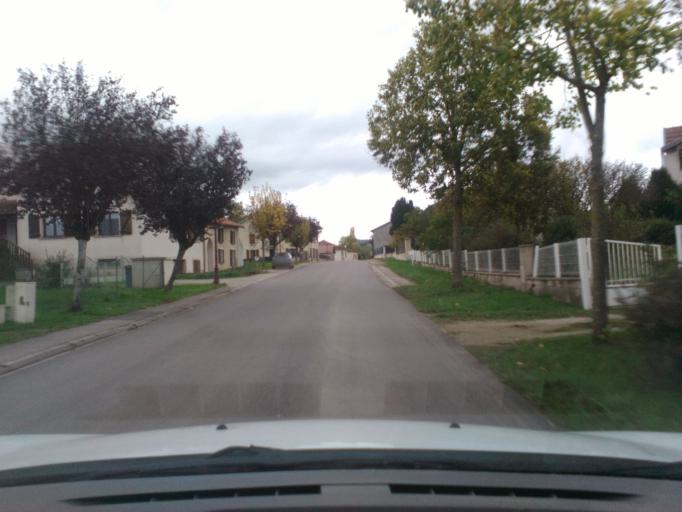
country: FR
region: Lorraine
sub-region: Departement des Vosges
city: Mirecourt
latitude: 48.3529
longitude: 6.0872
